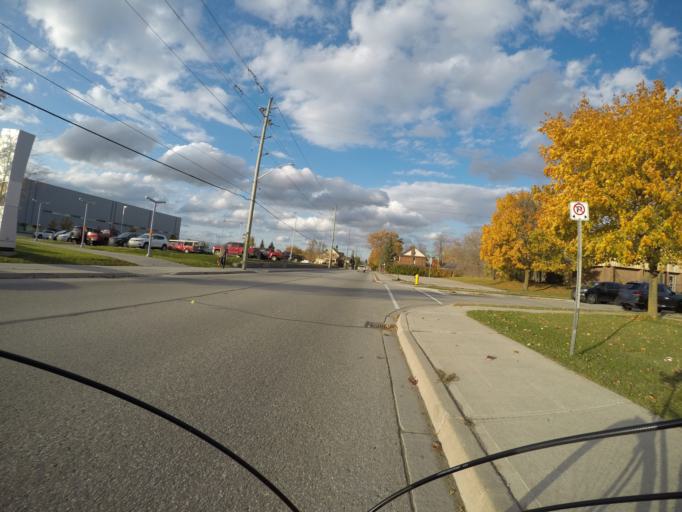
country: CA
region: Ontario
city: Waterloo
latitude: 43.5956
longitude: -80.5638
